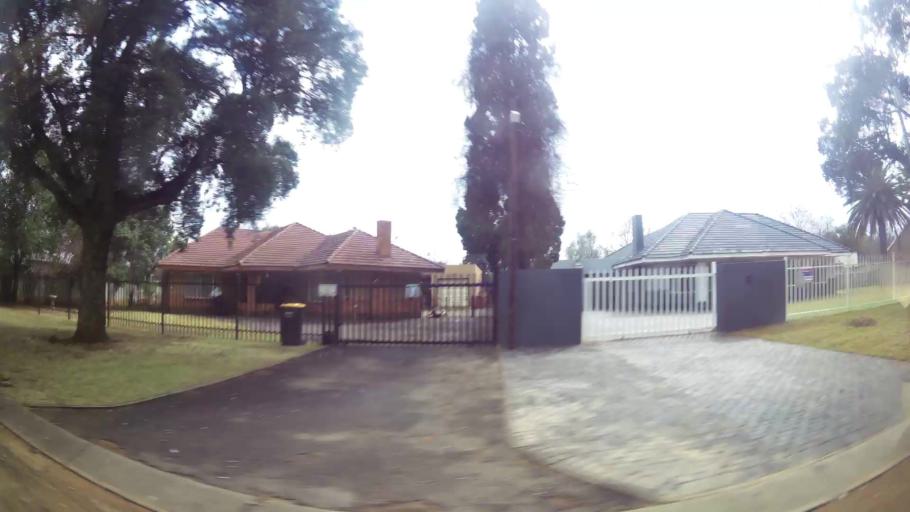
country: ZA
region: Gauteng
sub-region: Sedibeng District Municipality
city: Vereeniging
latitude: -26.6496
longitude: 27.9728
